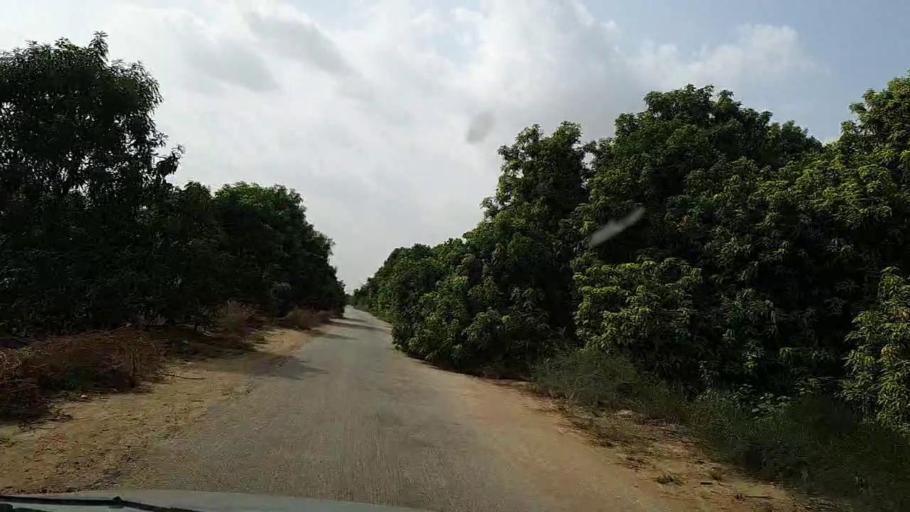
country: PK
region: Sindh
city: Kotri
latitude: 25.2503
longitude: 68.2590
